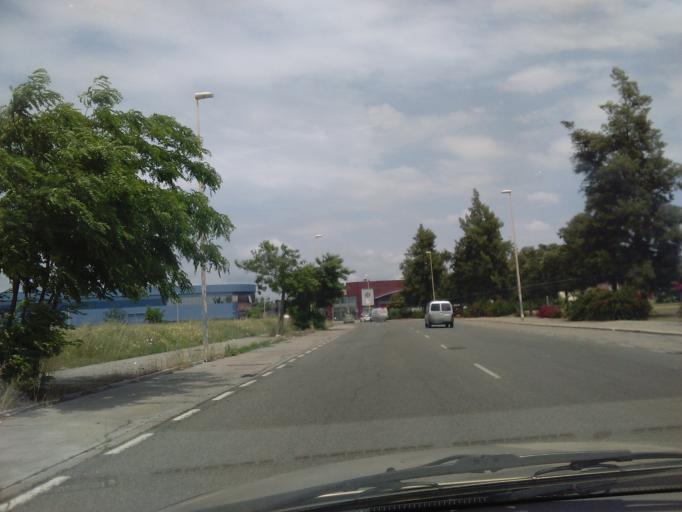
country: ES
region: Andalusia
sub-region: Provincia de Sevilla
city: Sevilla
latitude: 37.3789
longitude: -5.9307
